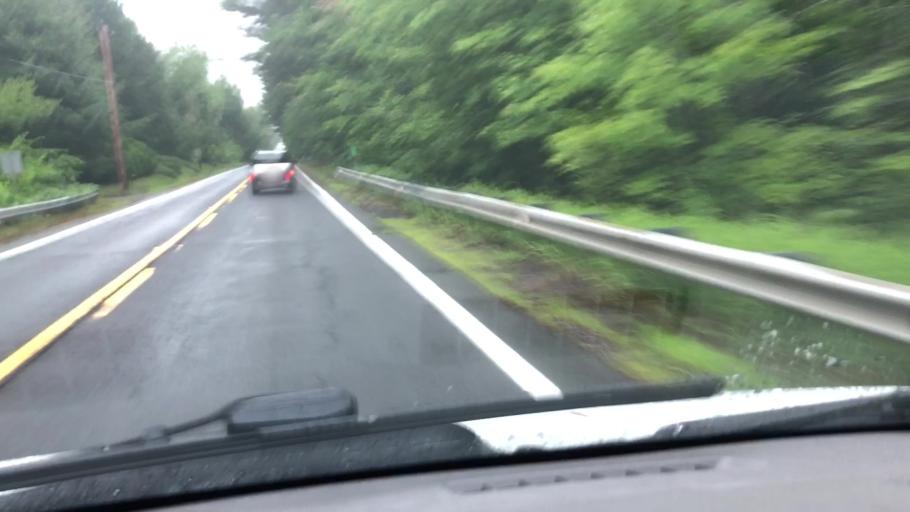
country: US
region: Massachusetts
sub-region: Hampshire County
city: Chesterfield
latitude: 42.3731
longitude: -72.9142
